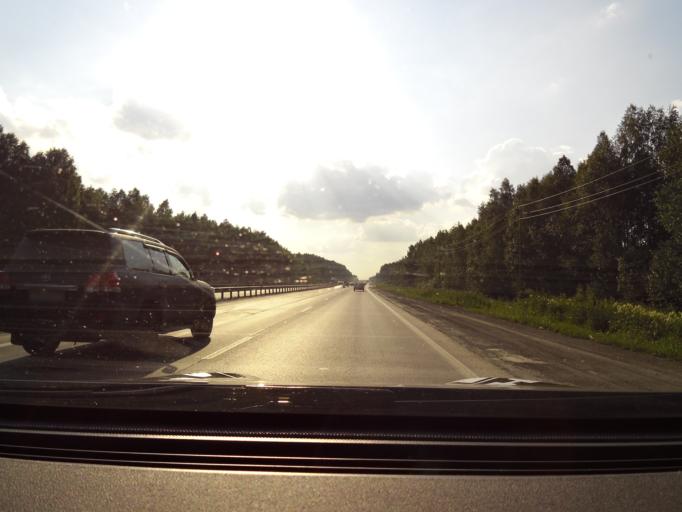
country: RU
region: Sverdlovsk
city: Severka
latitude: 56.8364
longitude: 60.2836
